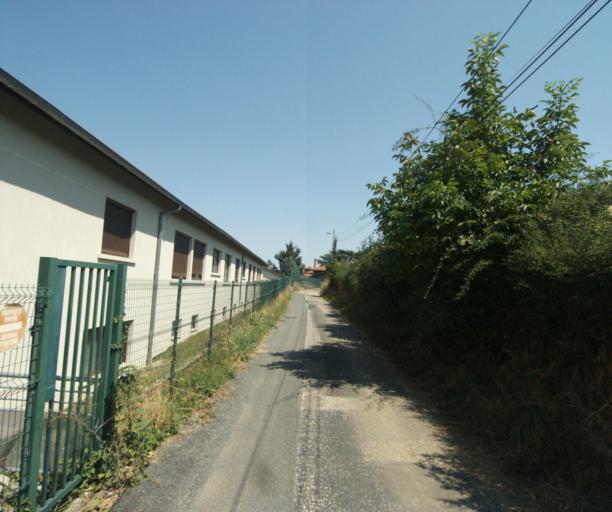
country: FR
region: Rhone-Alpes
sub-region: Departement du Rhone
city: Sain-Bel
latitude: 45.7996
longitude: 4.6024
